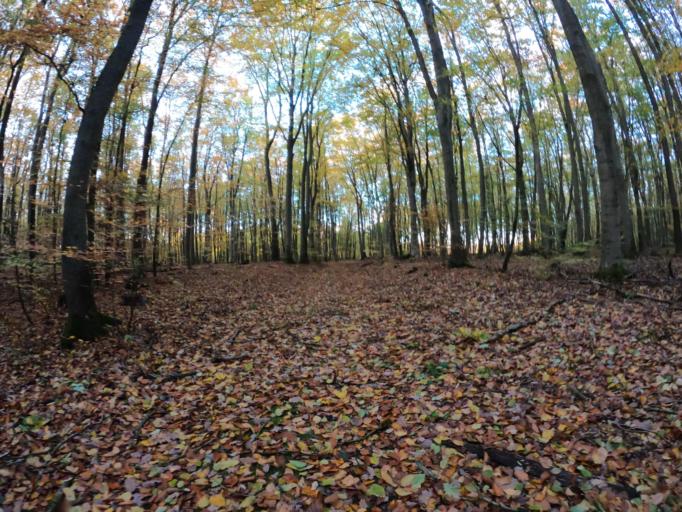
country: PL
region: West Pomeranian Voivodeship
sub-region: Powiat mysliborski
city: Barlinek
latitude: 52.9685
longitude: 15.2315
